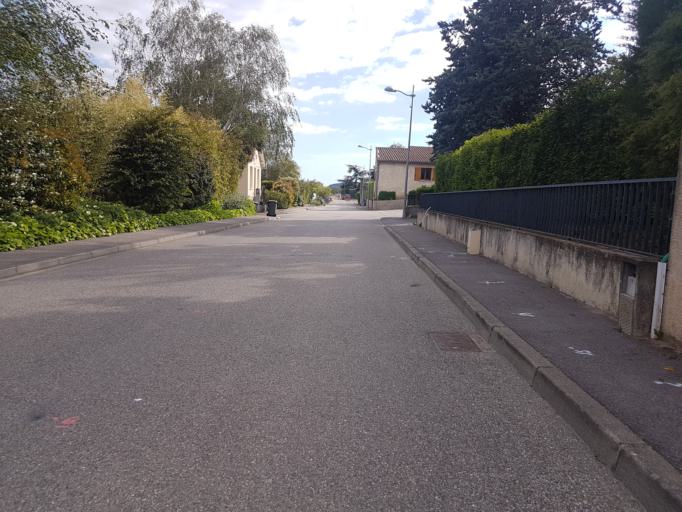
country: FR
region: Rhone-Alpes
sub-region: Departement de l'Ardeche
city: Guilherand-Granges
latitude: 44.9224
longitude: 4.8673
